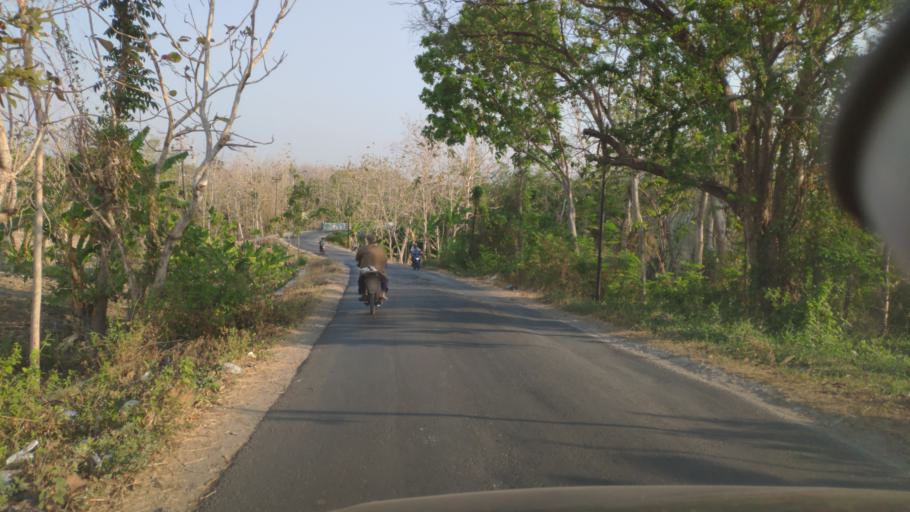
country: ID
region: Central Java
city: Jeponkrajan
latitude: -6.9832
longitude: 111.4811
